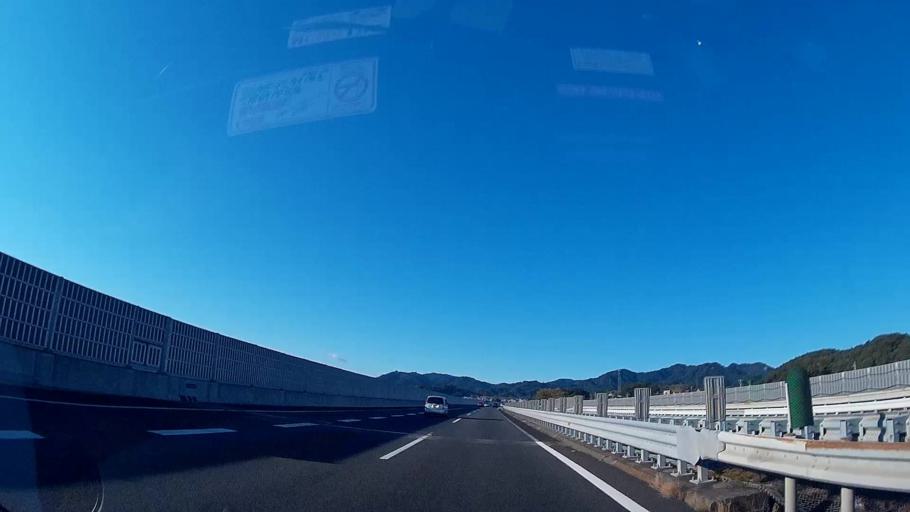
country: JP
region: Tokyo
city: Hachioji
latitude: 35.6612
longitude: 139.2852
